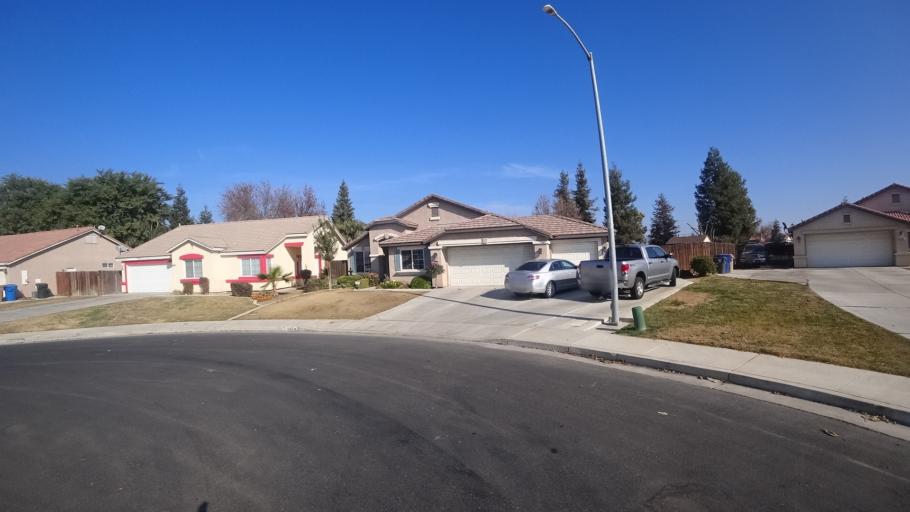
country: US
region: California
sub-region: Kern County
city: Greenacres
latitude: 35.3113
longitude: -119.1114
